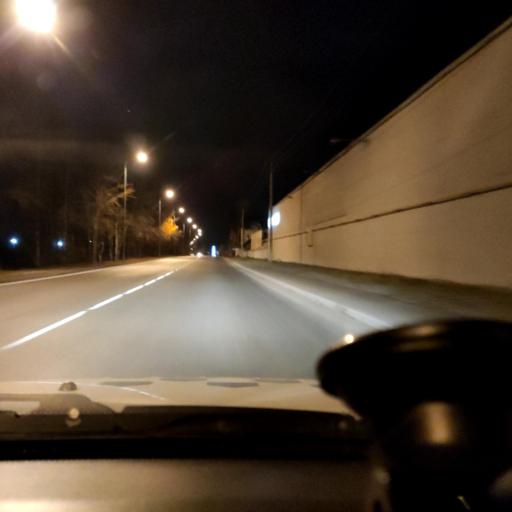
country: RU
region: Perm
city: Perm
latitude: 58.0887
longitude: 56.3115
